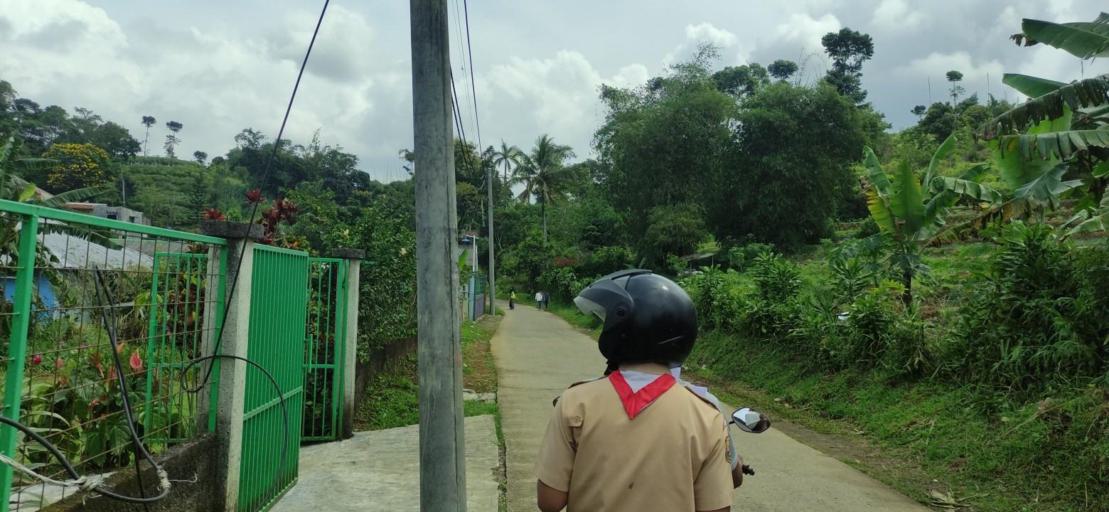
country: ID
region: West Java
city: Caringin
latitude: -6.6428
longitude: 106.8891
